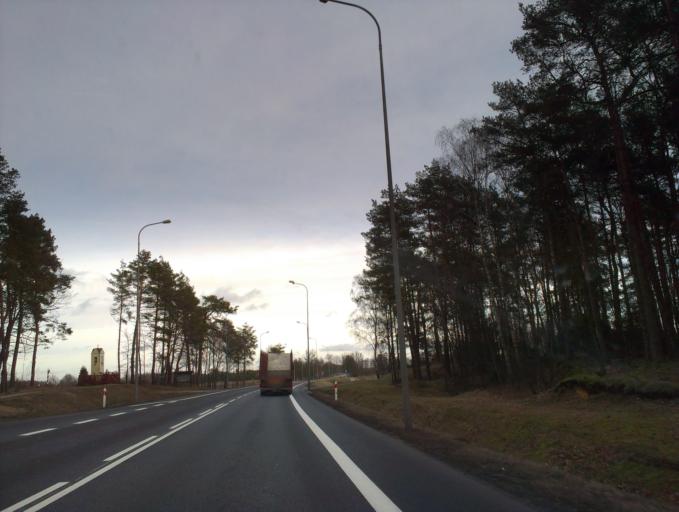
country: PL
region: Kujawsko-Pomorskie
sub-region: Powiat lipnowski
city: Skepe
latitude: 52.8871
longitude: 19.3989
